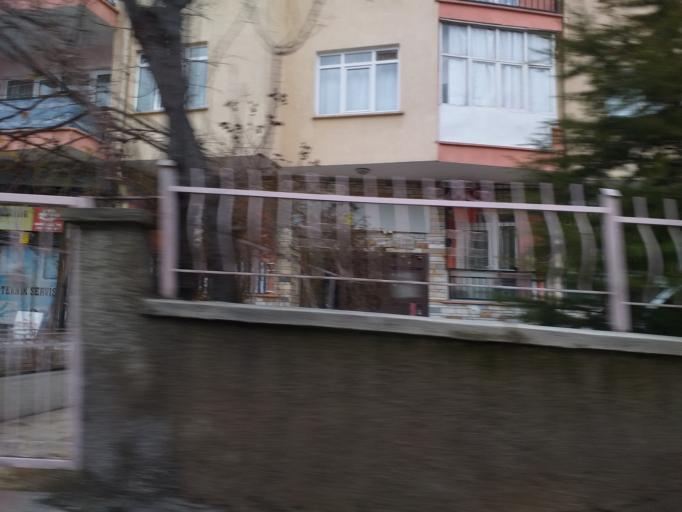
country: TR
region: Ankara
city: Ankara
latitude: 39.9780
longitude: 32.8300
